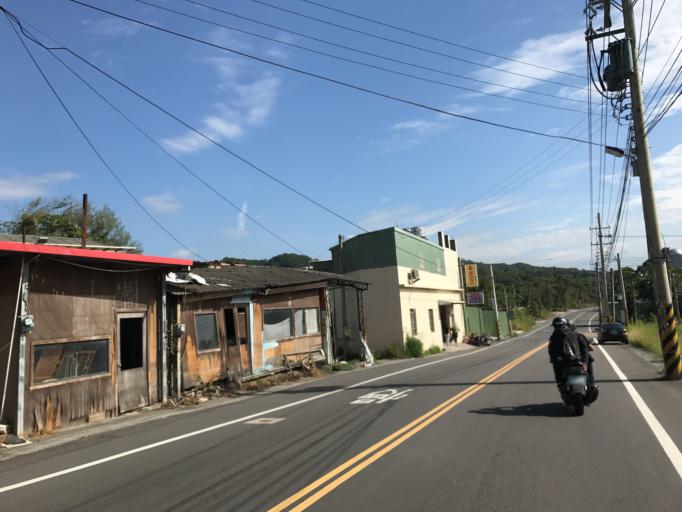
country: TW
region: Taiwan
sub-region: Hsinchu
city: Hsinchu
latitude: 24.7701
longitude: 120.9742
